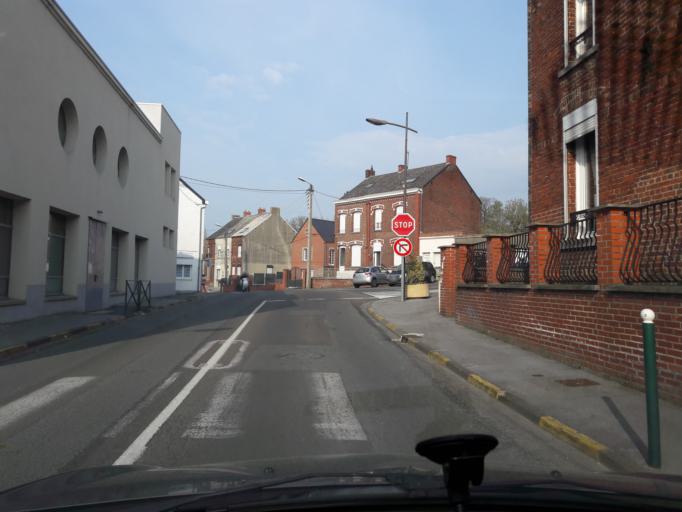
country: FR
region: Nord-Pas-de-Calais
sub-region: Departement du Nord
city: Rousies
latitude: 50.2726
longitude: 4.0057
